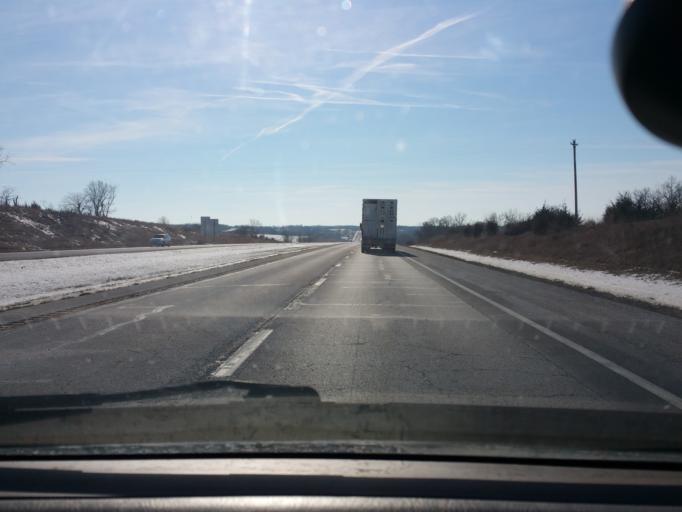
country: US
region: Missouri
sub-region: Harrison County
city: Bethany
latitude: 40.2470
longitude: -94.0130
